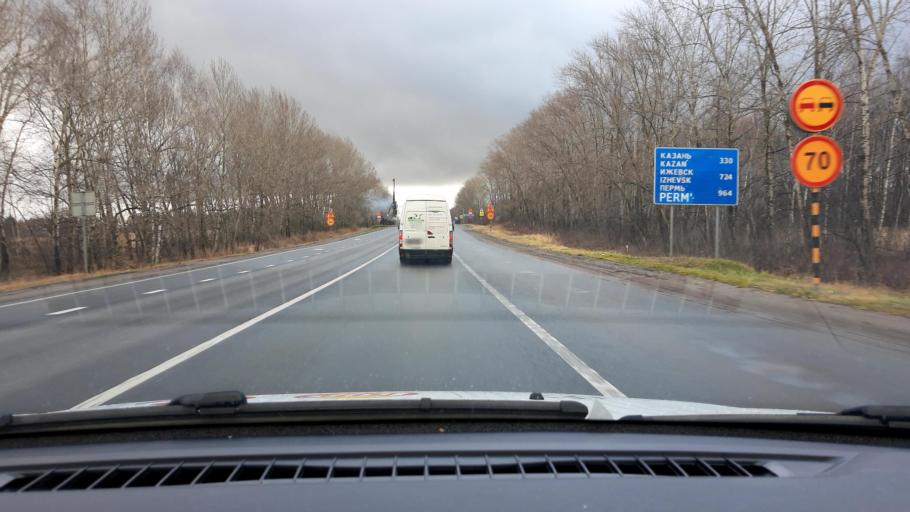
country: RU
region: Nizjnij Novgorod
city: Pamyat' Parizhskoy Kommuny
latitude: 56.0022
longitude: 44.6342
